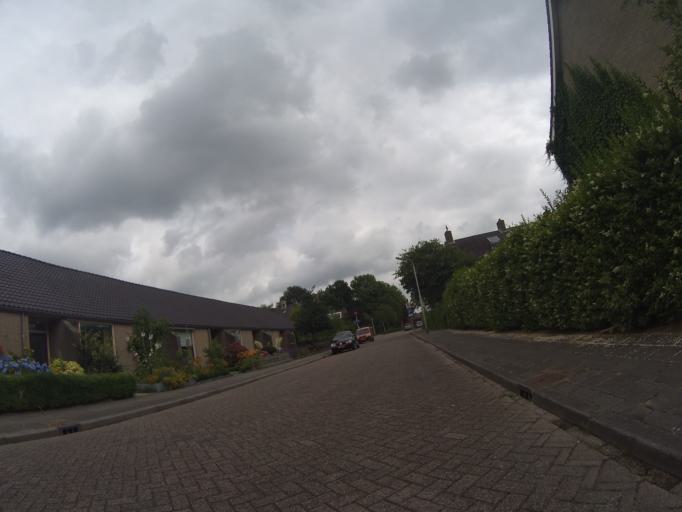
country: NL
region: Utrecht
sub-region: Gemeente Amersfoort
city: Amersfoort
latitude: 52.1707
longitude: 5.3910
